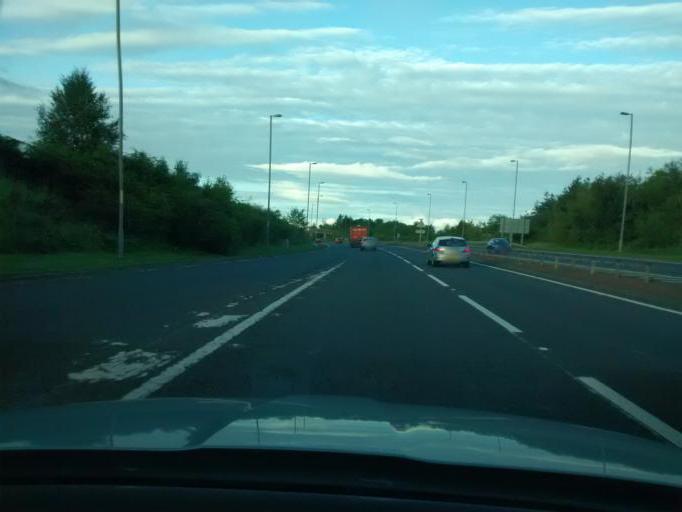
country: GB
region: Scotland
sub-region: Renfrewshire
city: Johnstone
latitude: 55.8331
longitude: -4.5311
